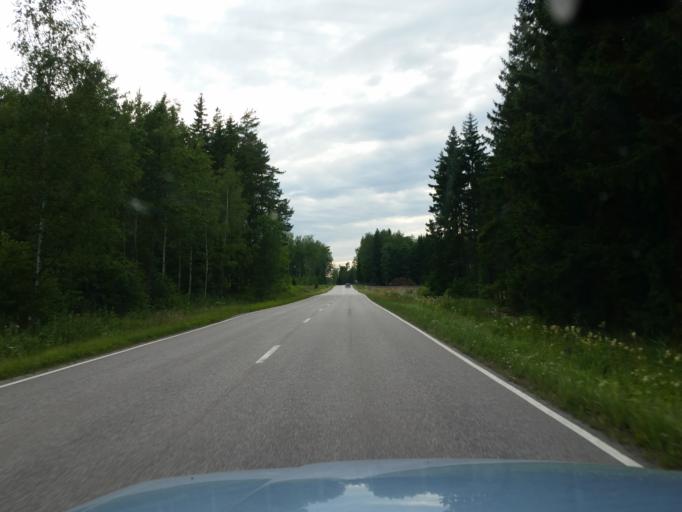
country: FI
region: Varsinais-Suomi
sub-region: Aboland-Turunmaa
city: Nagu
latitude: 60.1884
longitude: 21.9946
